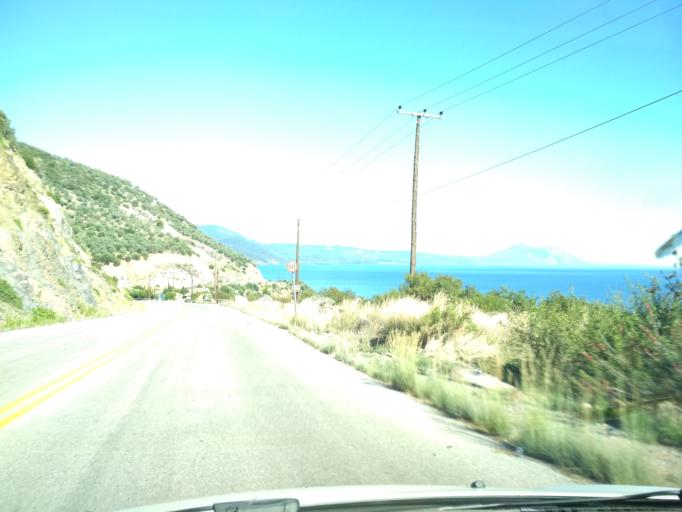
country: GR
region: Central Greece
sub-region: Nomos Evvoias
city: Oreoi
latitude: 38.8421
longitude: 23.0910
